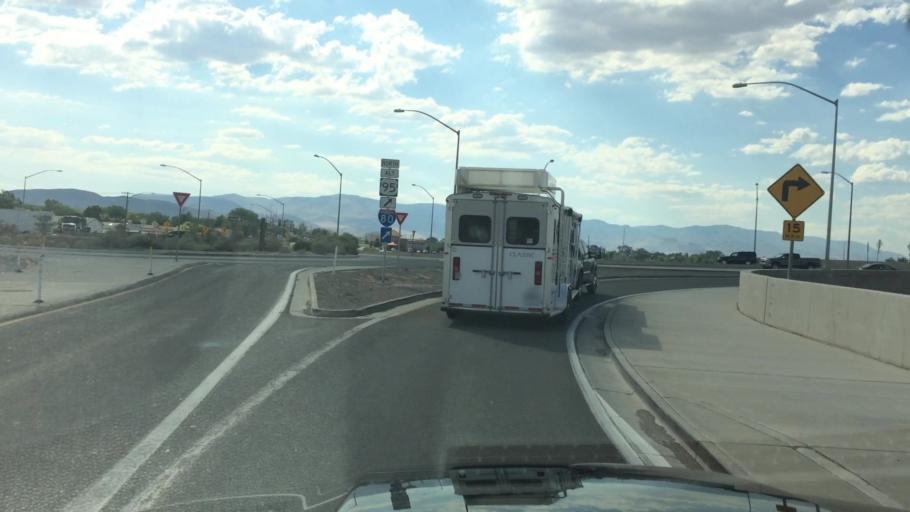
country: US
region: Nevada
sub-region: Lyon County
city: Fernley
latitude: 39.6035
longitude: -119.2262
